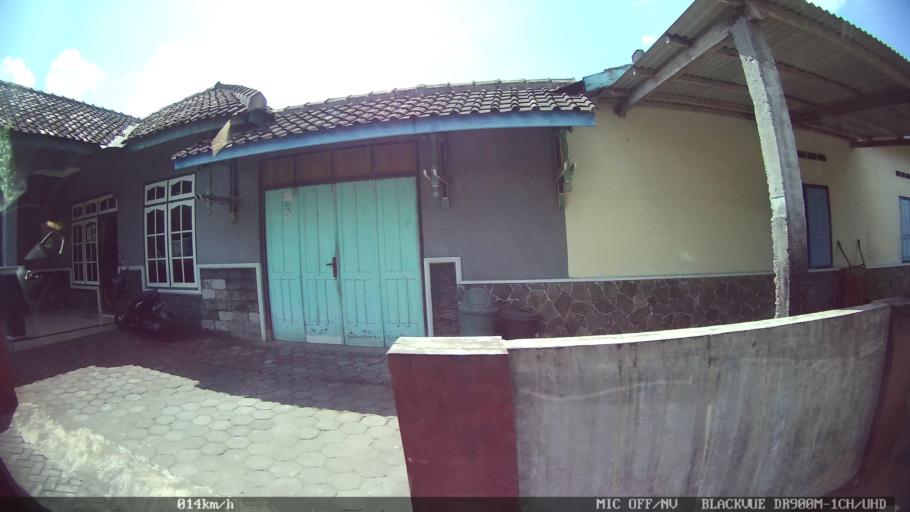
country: ID
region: Daerah Istimewa Yogyakarta
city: Sewon
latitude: -7.8414
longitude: 110.3830
